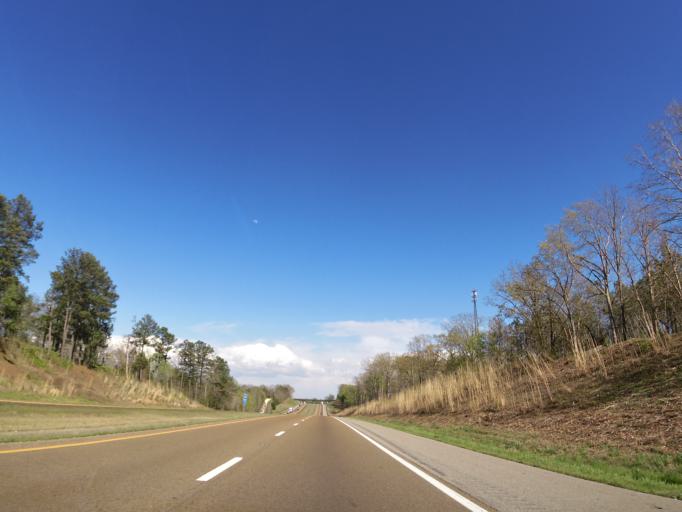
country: US
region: Tennessee
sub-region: Decatur County
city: Parsons
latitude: 35.8194
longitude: -88.1611
